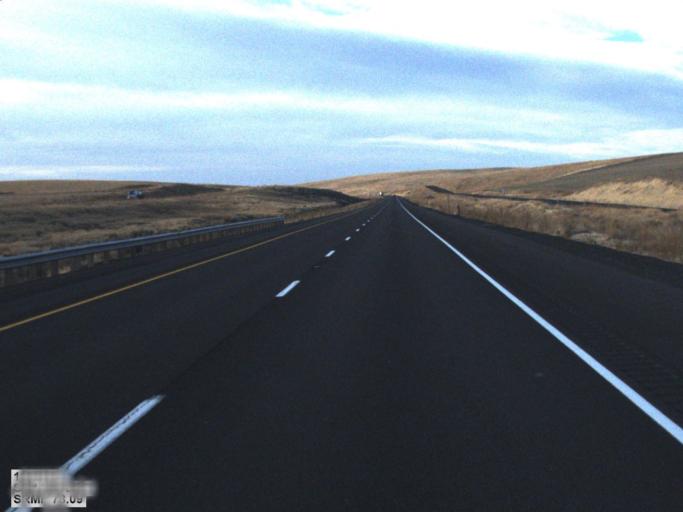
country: US
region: Washington
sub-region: Adams County
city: Ritzville
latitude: 46.9168
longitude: -118.6038
